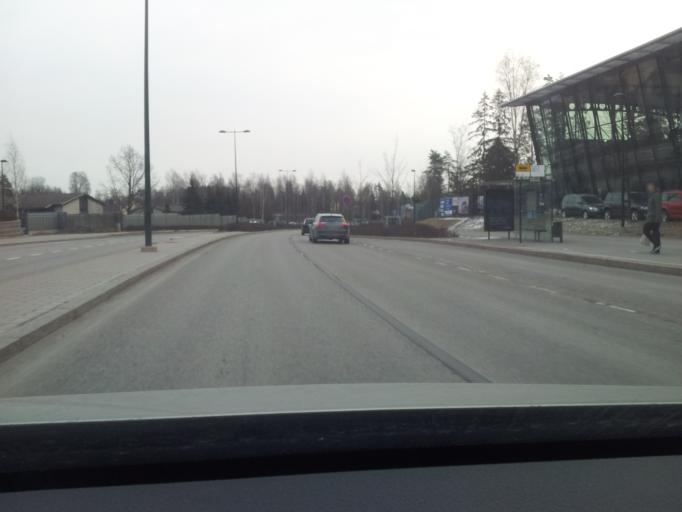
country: FI
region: Uusimaa
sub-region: Helsinki
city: Koukkuniemi
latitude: 60.1685
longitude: 24.7435
